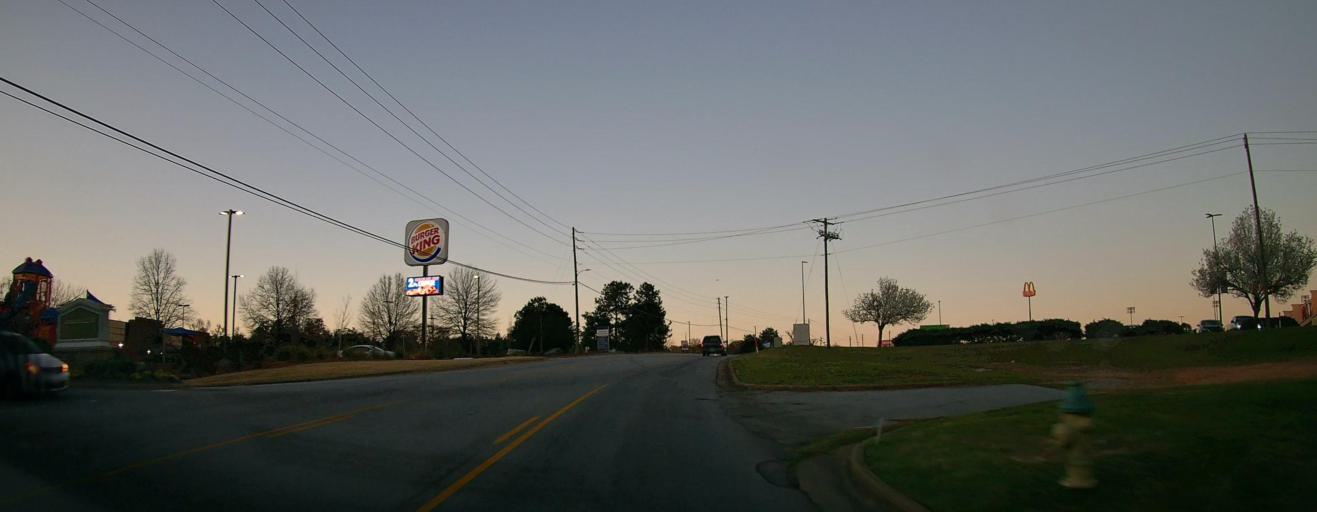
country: US
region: Alabama
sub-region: Russell County
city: Phenix City
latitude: 32.4954
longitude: -85.0185
